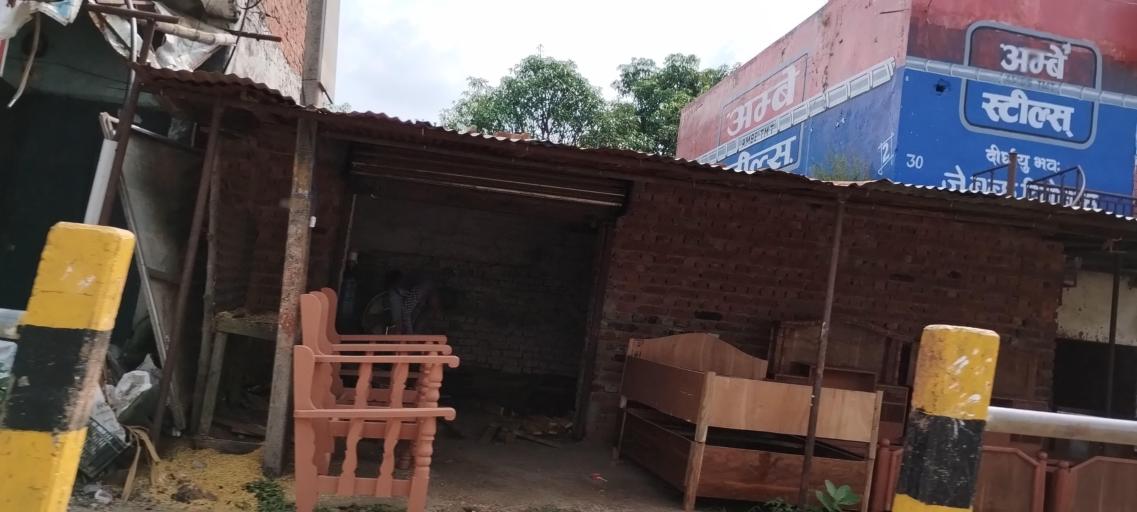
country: NP
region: Mid Western
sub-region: Bheri Zone
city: Nepalgunj
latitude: 28.1007
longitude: 81.6553
